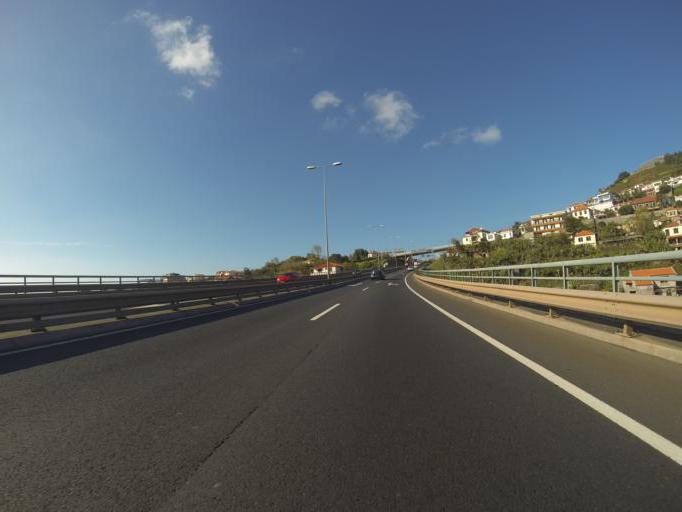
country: PT
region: Madeira
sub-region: Funchal
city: Nossa Senhora do Monte
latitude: 32.6593
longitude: -16.9341
